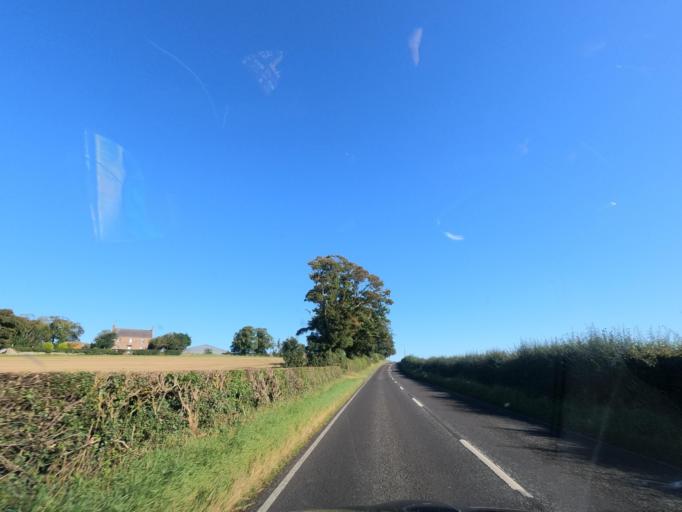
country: GB
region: England
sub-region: Northumberland
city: Ford
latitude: 55.7285
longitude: -2.0949
